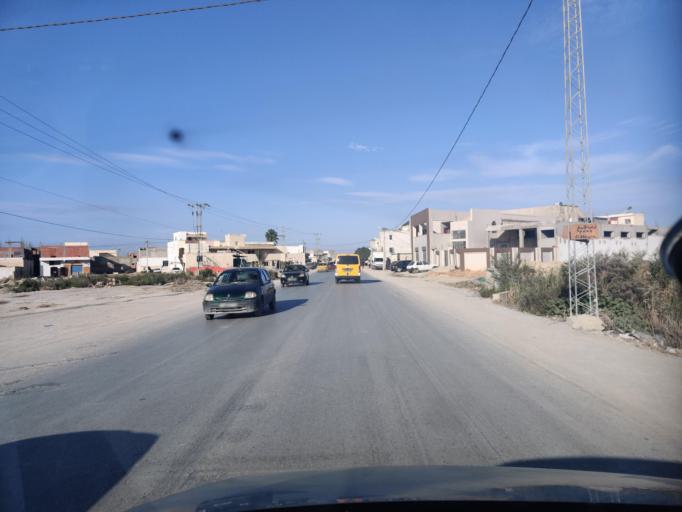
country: TN
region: Ariana
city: Ariana
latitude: 36.9562
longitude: 10.2166
